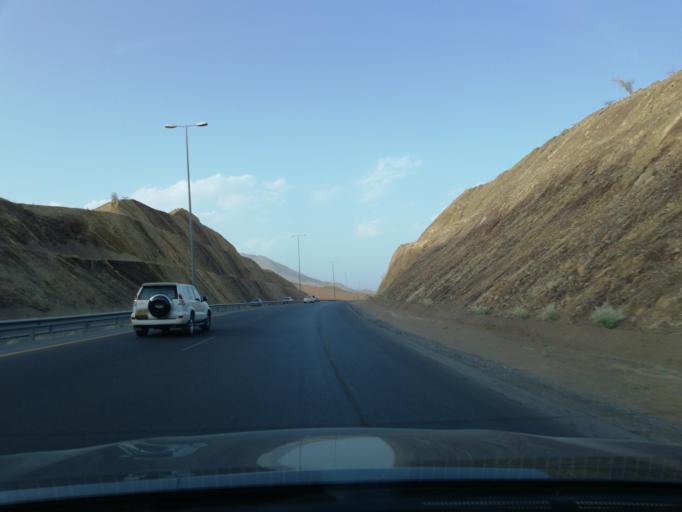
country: OM
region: Muhafazat ad Dakhiliyah
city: Izki
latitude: 22.8954
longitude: 57.7176
